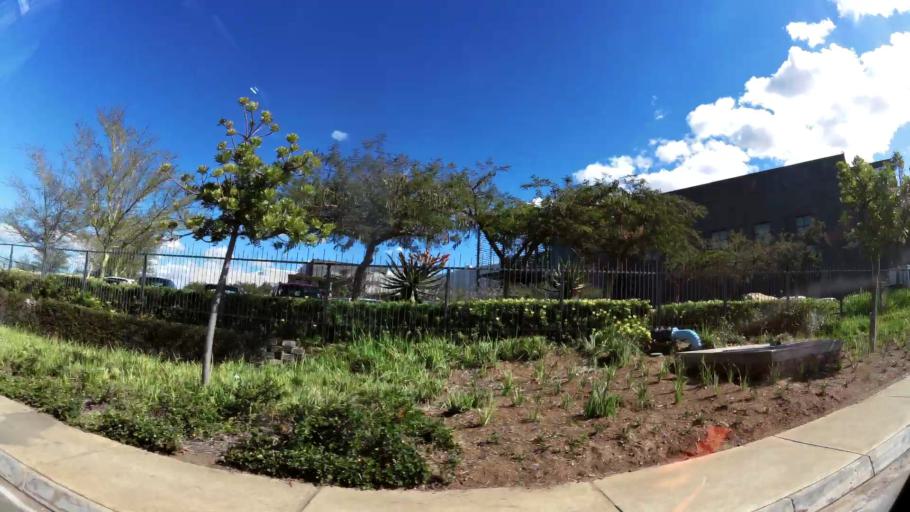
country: ZA
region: Limpopo
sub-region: Capricorn District Municipality
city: Polokwane
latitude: -23.8726
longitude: 29.5109
